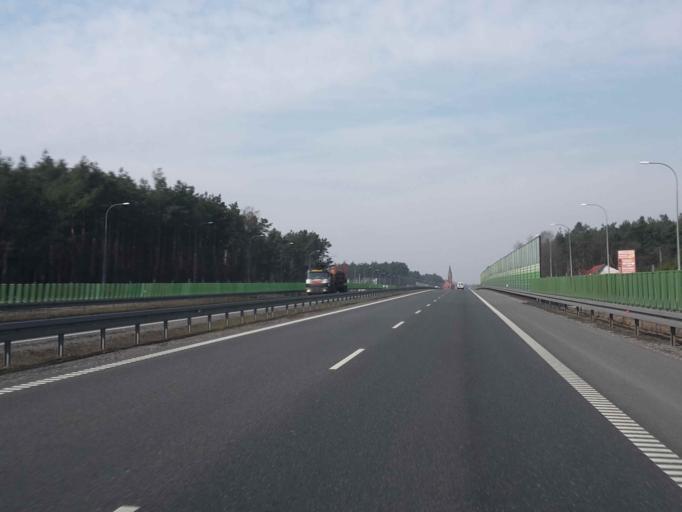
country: PL
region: Kujawsko-Pomorskie
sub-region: Powiat bydgoski
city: Biale Blota
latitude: 53.0675
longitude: 17.9357
